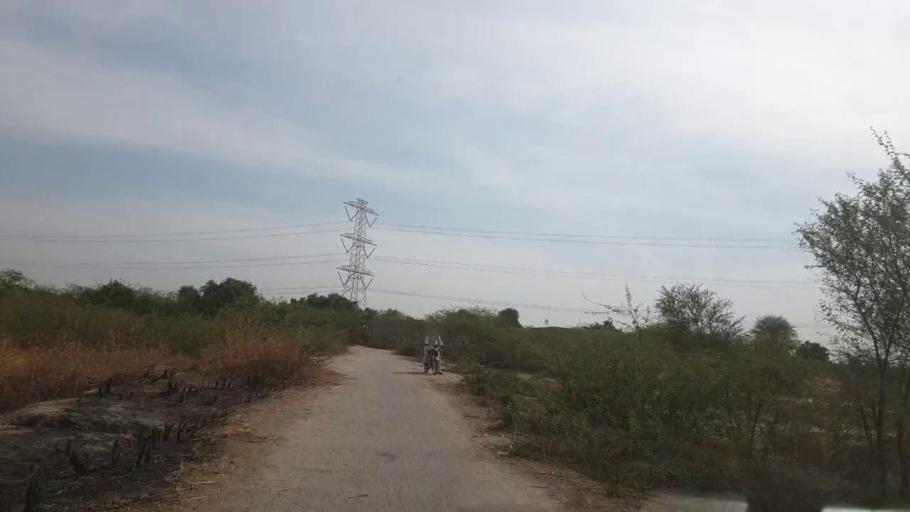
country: PK
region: Sindh
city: Nabisar
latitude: 25.0436
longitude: 69.5685
